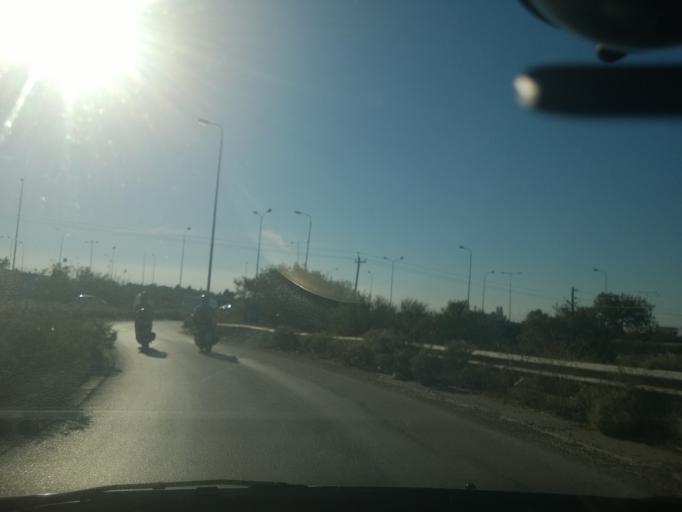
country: GR
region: Central Macedonia
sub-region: Nomos Thessalonikis
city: Thermi
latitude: 40.5402
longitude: 23.0091
